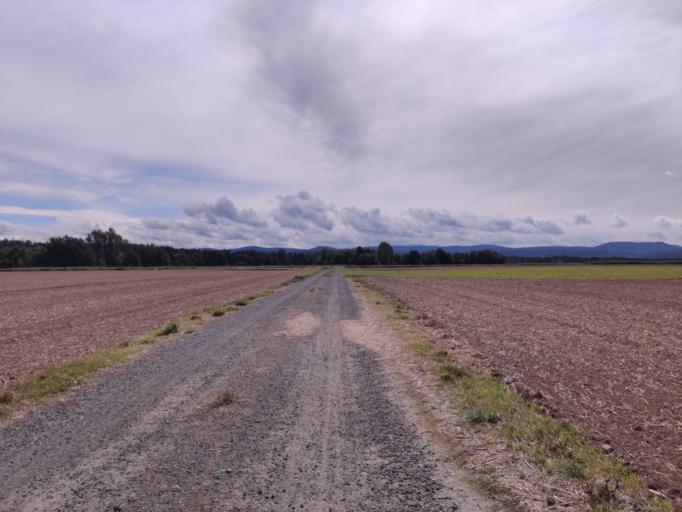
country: DE
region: Lower Saxony
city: Langelsheim
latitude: 51.9825
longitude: 10.3670
